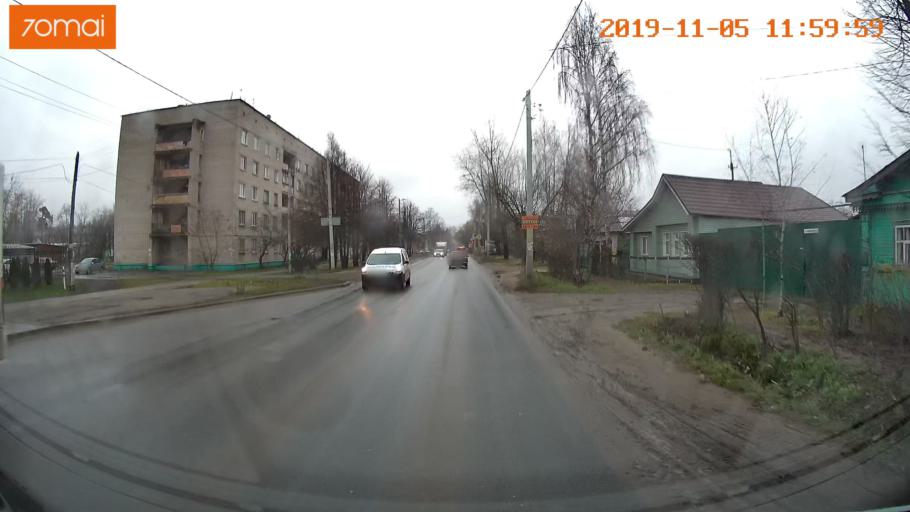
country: RU
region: Ivanovo
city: Kokhma
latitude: 56.9768
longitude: 41.0491
